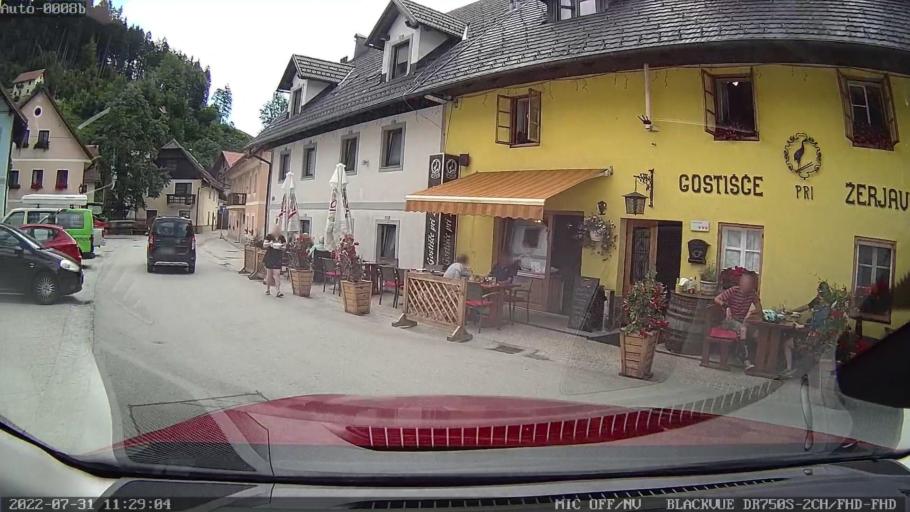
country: AT
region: Carinthia
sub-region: Politischer Bezirk Villach Land
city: Arnoldstein
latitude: 46.4976
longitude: 13.7172
